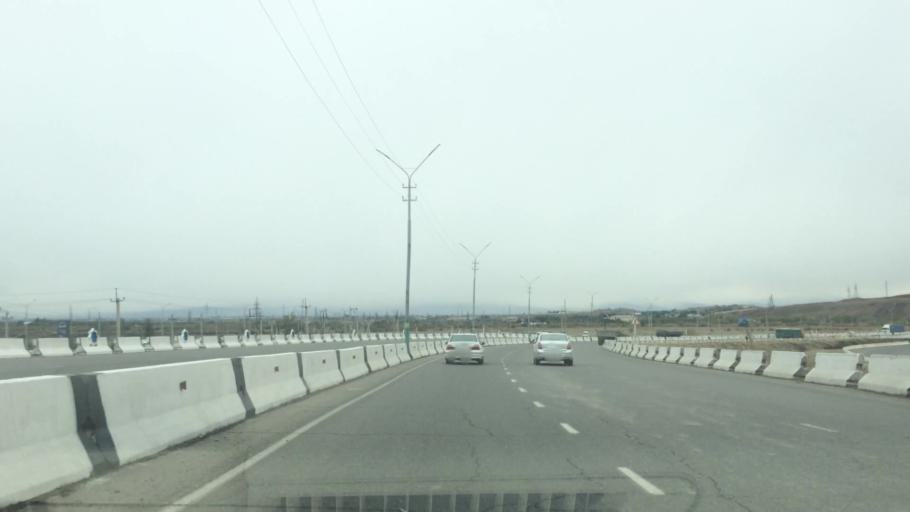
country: UZ
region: Samarqand
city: Jomboy
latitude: 39.6927
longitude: 67.0678
